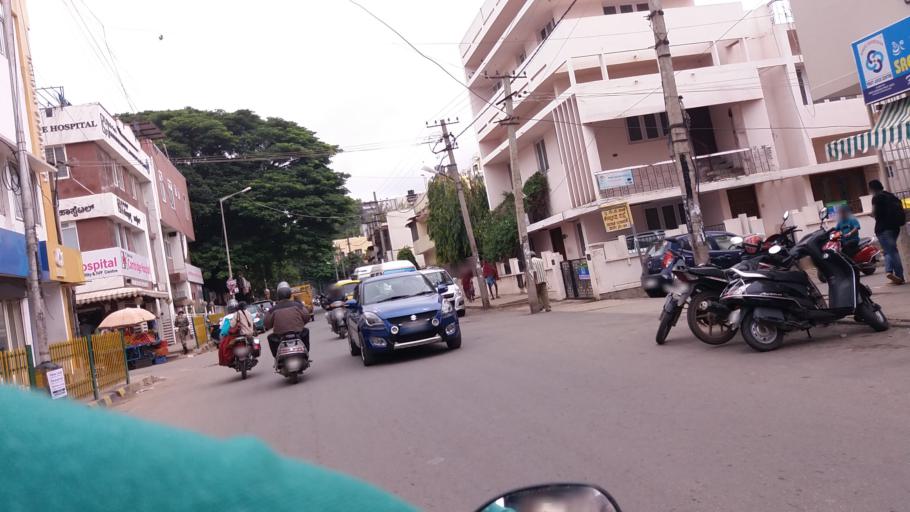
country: IN
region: Karnataka
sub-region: Bangalore Urban
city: Bangalore
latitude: 12.9714
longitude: 77.6277
